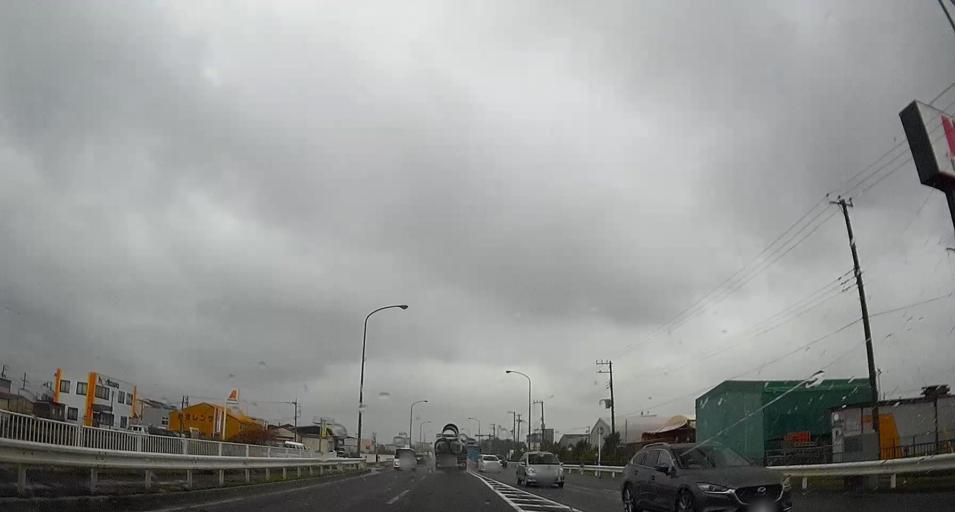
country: JP
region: Chiba
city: Ichihara
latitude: 35.5457
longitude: 140.1203
